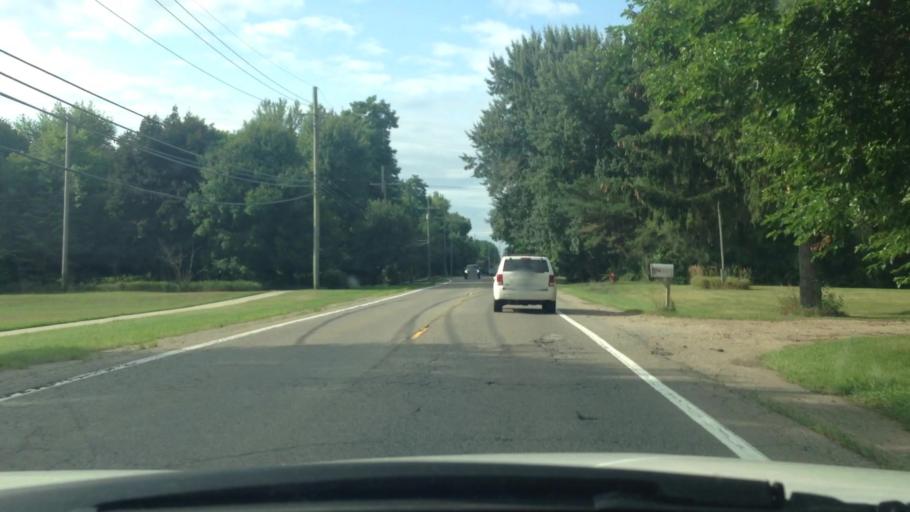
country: US
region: Michigan
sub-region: Oakland County
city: Waterford
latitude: 42.7100
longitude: -83.3489
